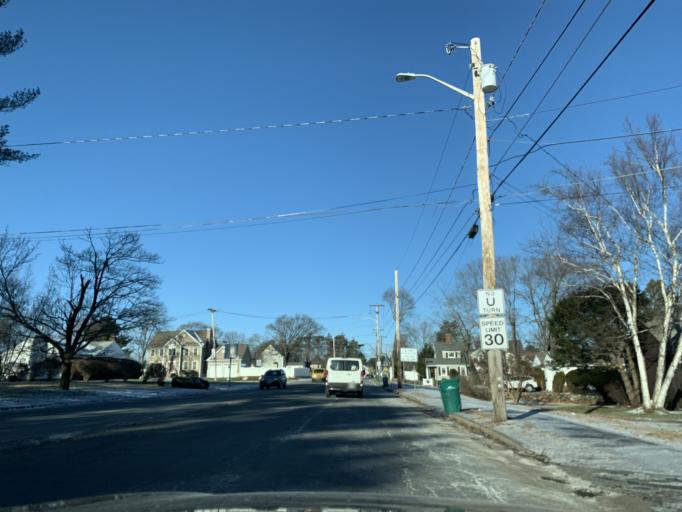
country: US
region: Massachusetts
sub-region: Norfolk County
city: Canton
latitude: 42.1730
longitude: -71.1738
